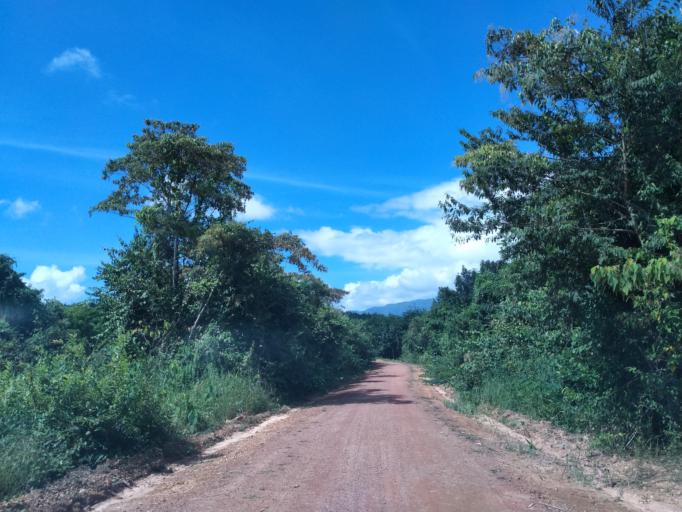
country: LA
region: Vientiane
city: Muang Phon-Hong
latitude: 18.6417
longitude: 102.8902
